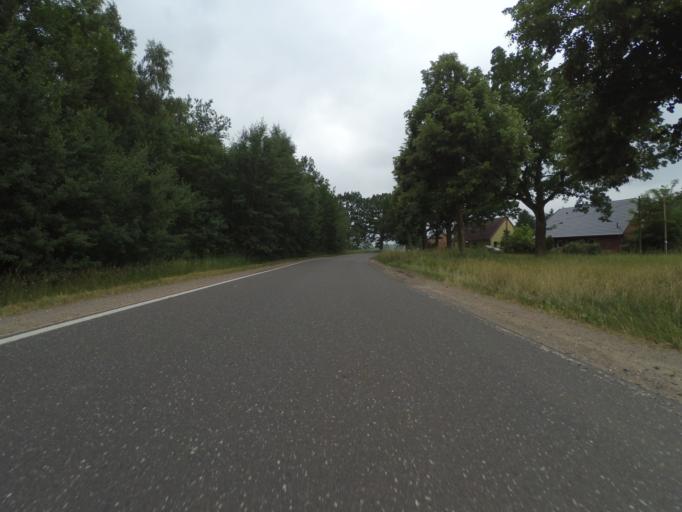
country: DE
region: Mecklenburg-Vorpommern
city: Spornitz
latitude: 53.4764
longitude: 11.6540
